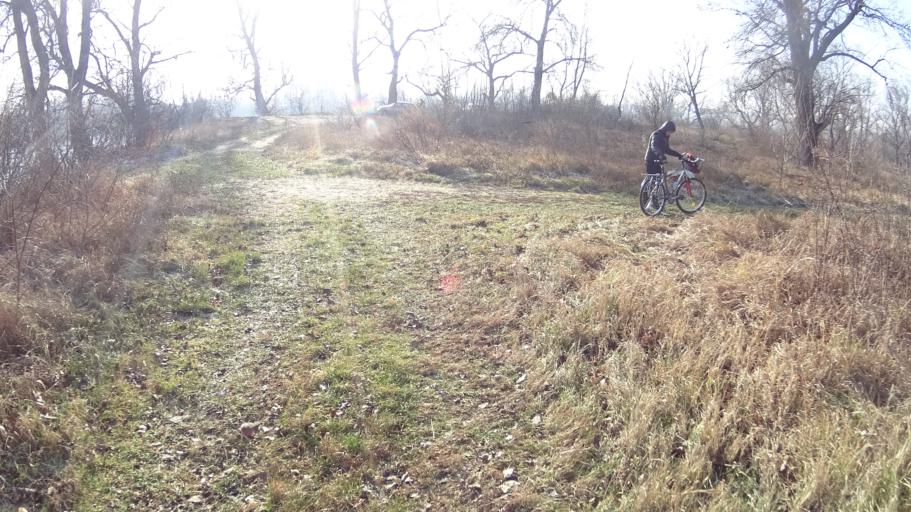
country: HU
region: Borsod-Abauj-Zemplen
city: Nyekladhaza
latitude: 47.9882
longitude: 20.8511
